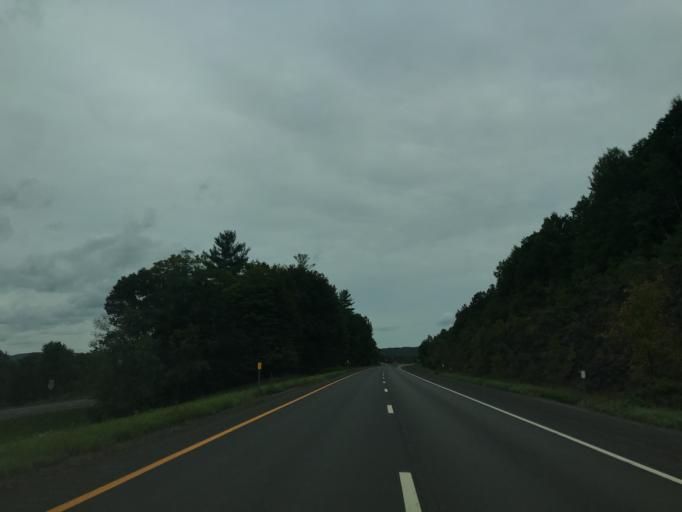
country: US
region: New York
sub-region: Delaware County
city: Sidney
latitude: 42.2924
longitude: -75.4194
